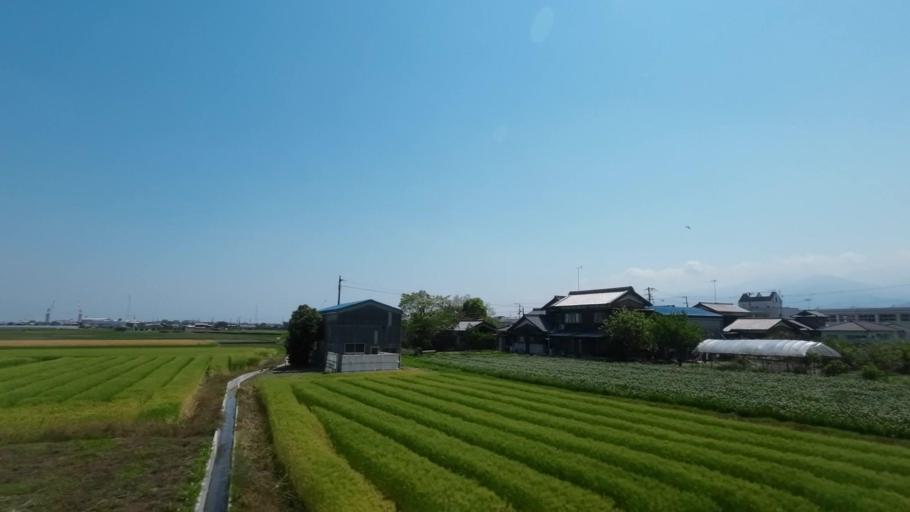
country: JP
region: Ehime
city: Saijo
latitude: 33.9141
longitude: 133.0988
